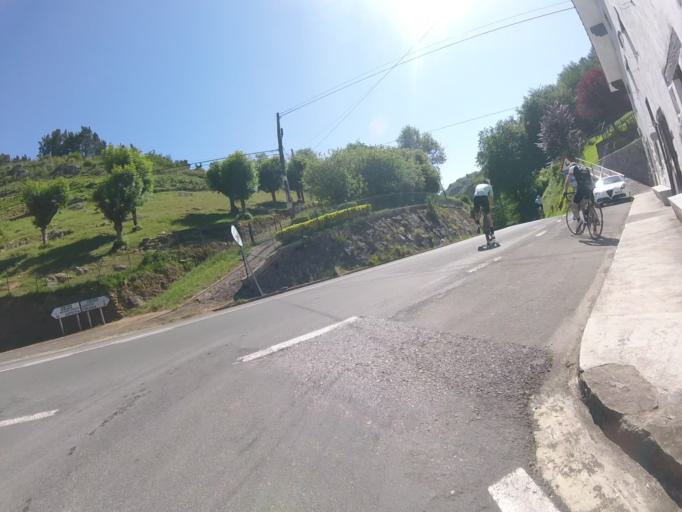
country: ES
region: Basque Country
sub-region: Provincia de Guipuzcoa
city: Albiztur
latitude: 43.1217
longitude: -2.1525
